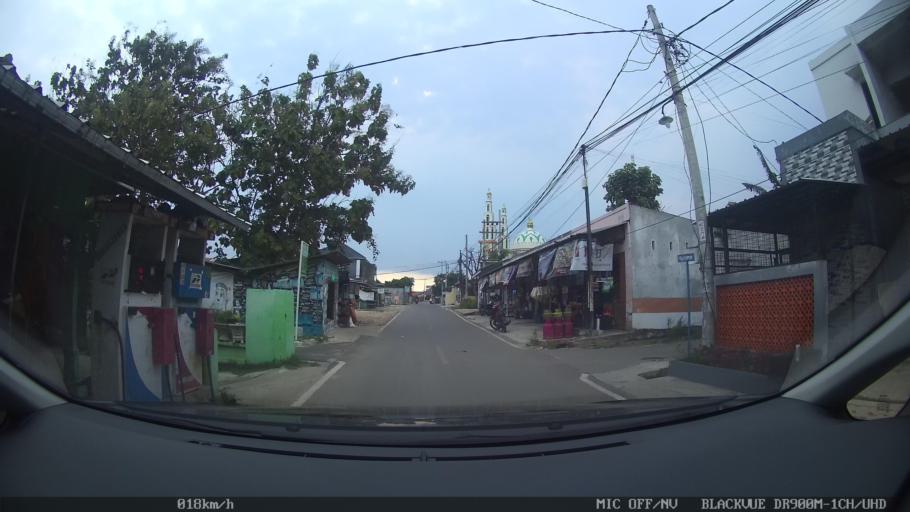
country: ID
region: Lampung
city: Kedaton
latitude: -5.3541
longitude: 105.2414
